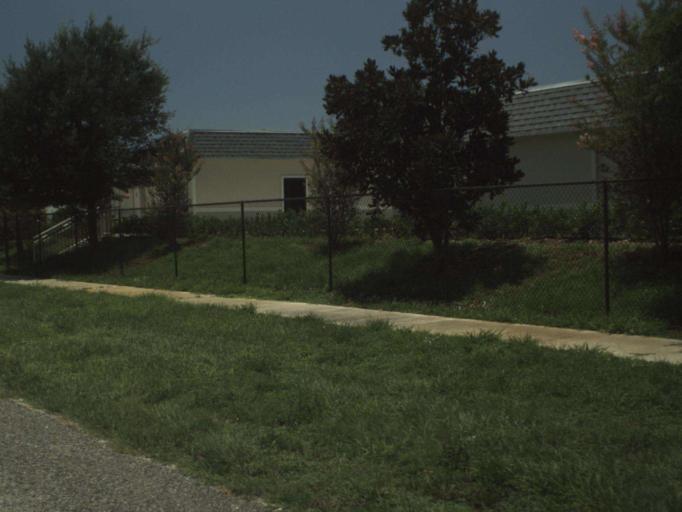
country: US
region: Florida
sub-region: Indian River County
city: Winter Beach
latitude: 27.7146
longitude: -80.4197
